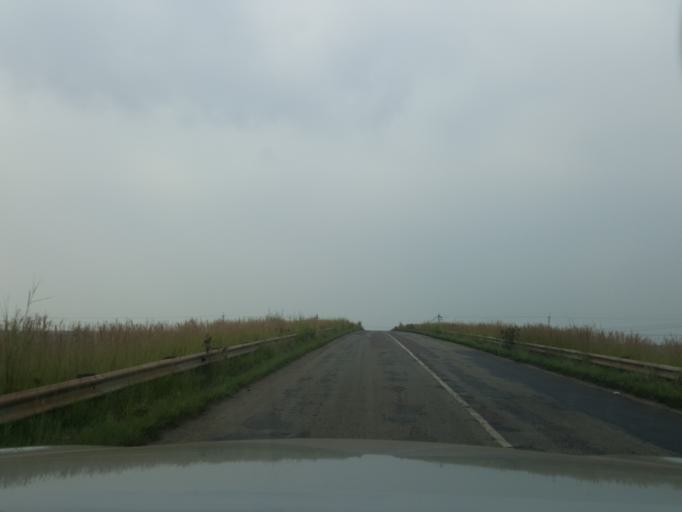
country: ZA
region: Mpumalanga
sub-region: Nkangala District Municipality
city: Middelburg
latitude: -26.0114
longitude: 29.4497
